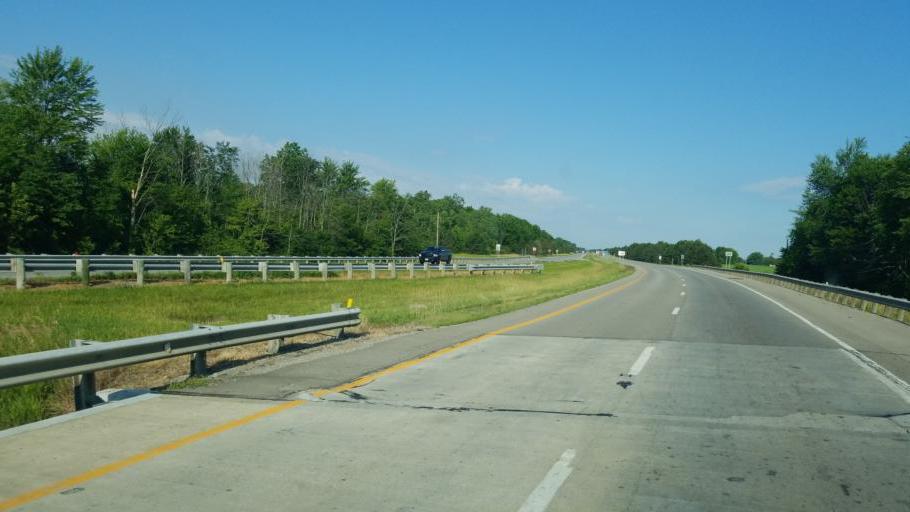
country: US
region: Ohio
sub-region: Wyandot County
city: Carey
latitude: 40.9818
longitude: -83.5014
